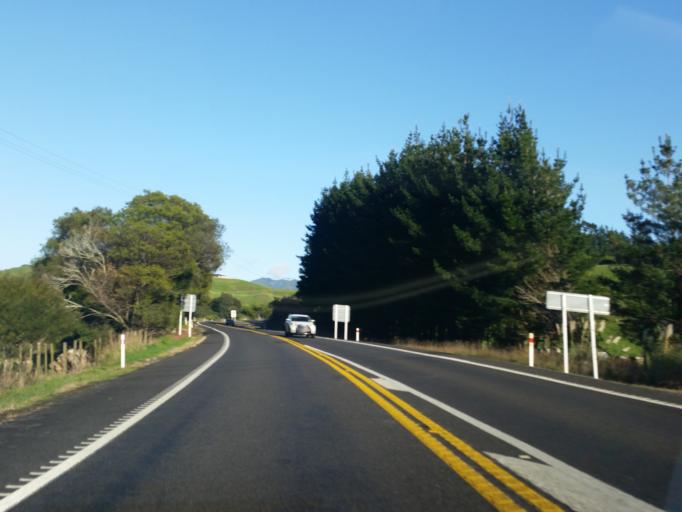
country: NZ
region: Bay of Plenty
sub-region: Western Bay of Plenty District
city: Katikati
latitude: -37.6489
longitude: 175.9744
